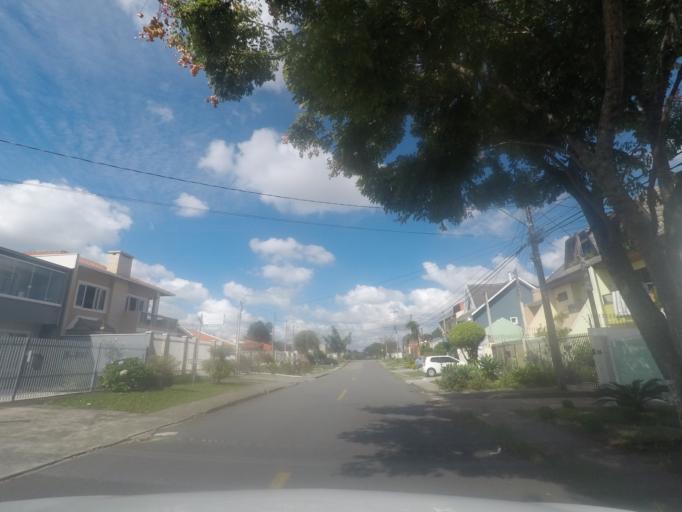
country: BR
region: Parana
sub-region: Pinhais
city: Pinhais
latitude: -25.4687
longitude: -49.2288
